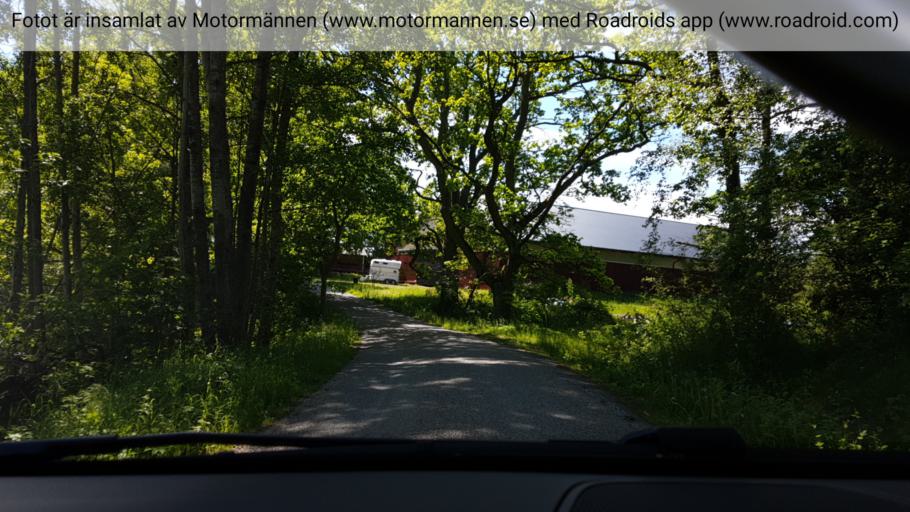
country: SE
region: Stockholm
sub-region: Haninge Kommun
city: Jordbro
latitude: 59.0157
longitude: 18.1144
